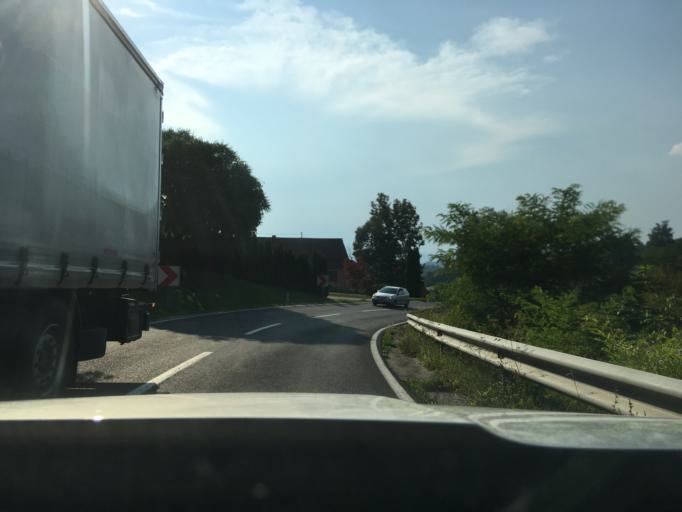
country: SI
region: Novo Mesto
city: Novo Mesto
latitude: 45.7498
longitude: 15.2032
